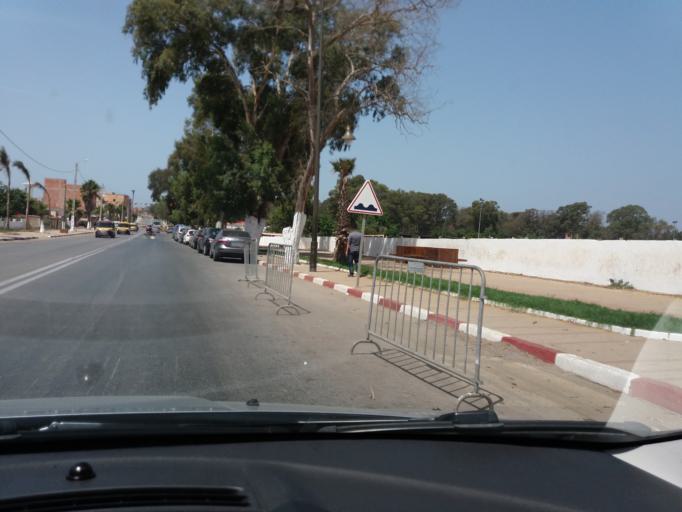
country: MA
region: Gharb-Chrarda-Beni Hssen
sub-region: Kenitra Province
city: Kenitra
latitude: 34.2661
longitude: -6.6468
